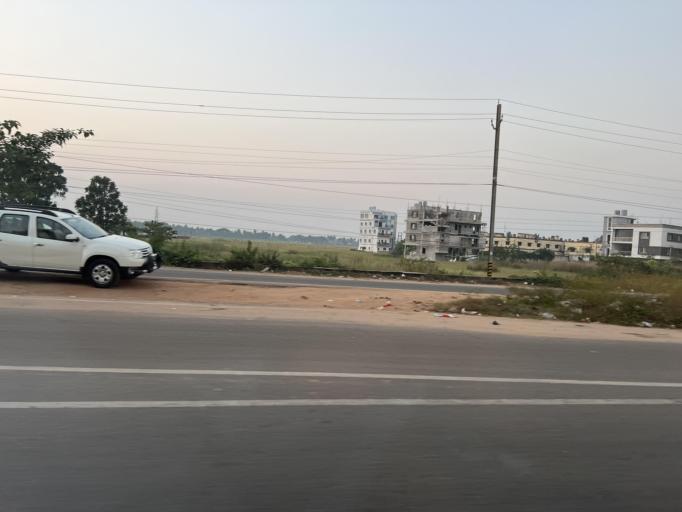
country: IN
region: Odisha
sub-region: Khordha
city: Bhubaneshwar
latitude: 20.3505
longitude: 85.8884
